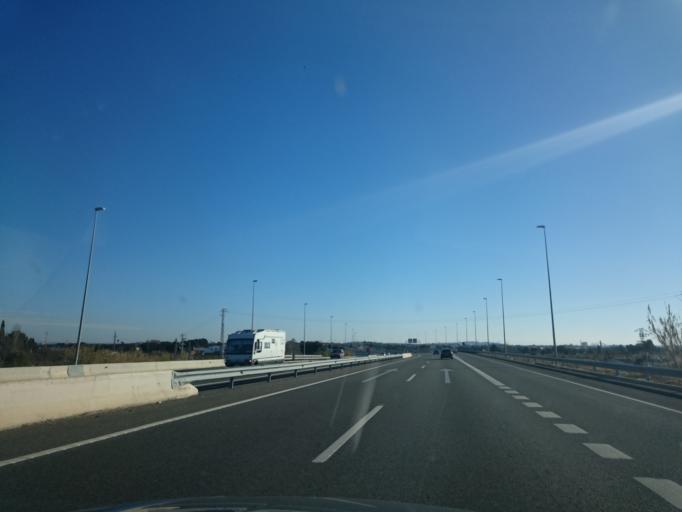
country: ES
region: Catalonia
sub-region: Provincia de Tarragona
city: Cambrils
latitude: 41.0834
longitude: 1.0690
